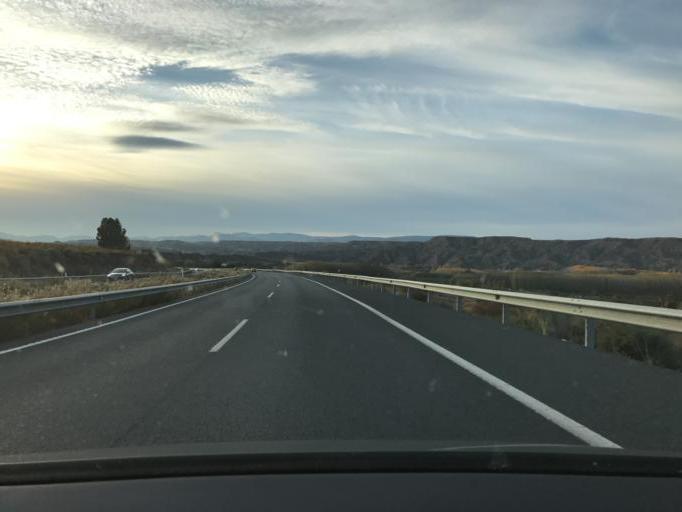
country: ES
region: Andalusia
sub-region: Provincia de Granada
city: Purullena
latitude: 37.3285
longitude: -3.1817
